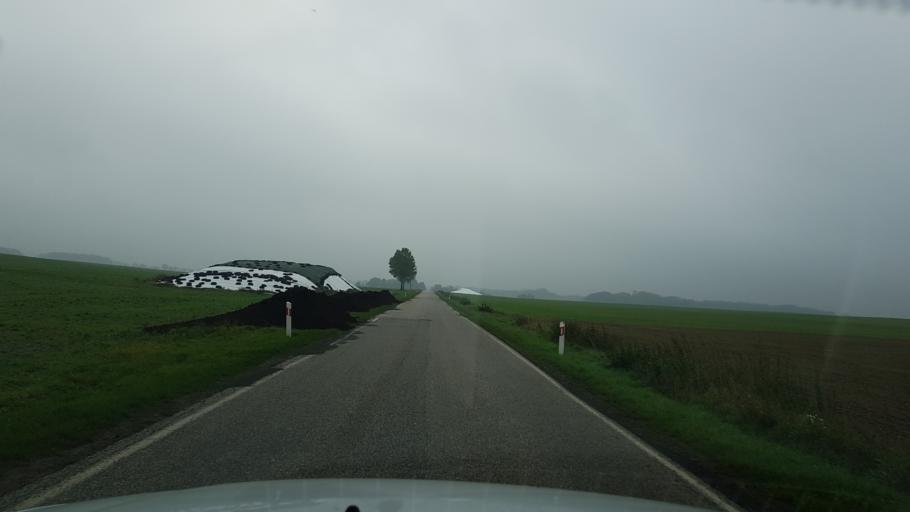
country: PL
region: West Pomeranian Voivodeship
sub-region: Powiat stargardzki
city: Dolice
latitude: 53.1702
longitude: 15.2206
